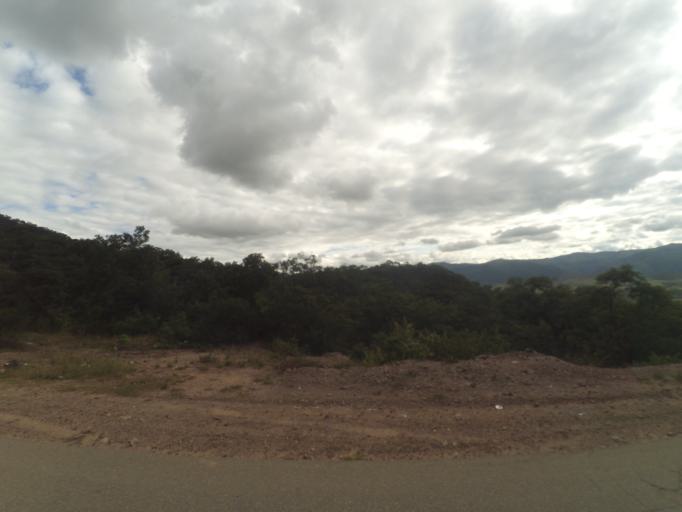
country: BO
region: Santa Cruz
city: Samaipata
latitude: -18.1663
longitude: -63.8990
